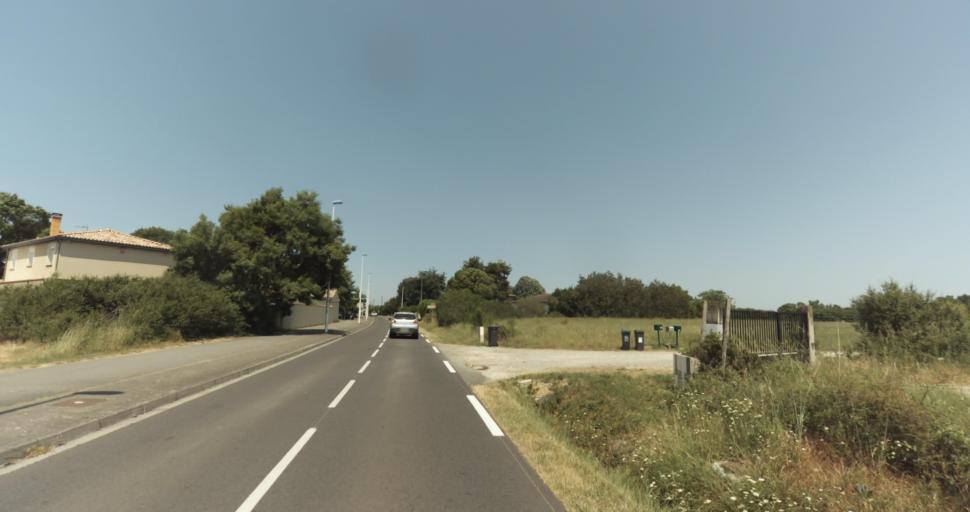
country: FR
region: Midi-Pyrenees
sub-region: Departement de la Haute-Garonne
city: Leguevin
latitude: 43.5960
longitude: 1.2463
